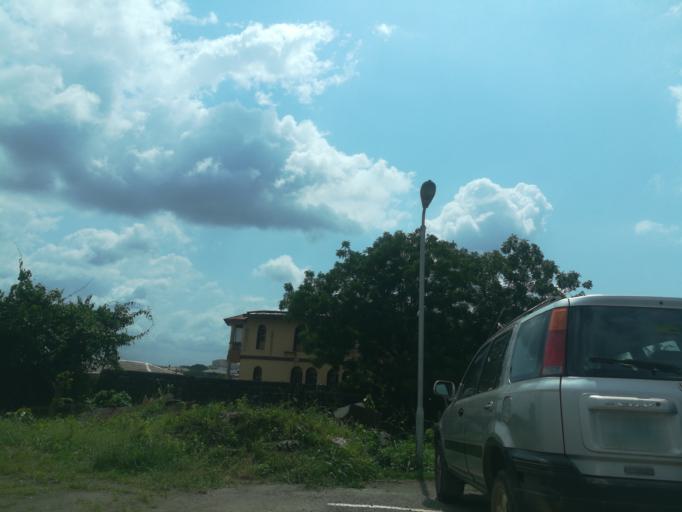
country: NG
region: Oyo
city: Ibadan
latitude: 7.3610
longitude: 3.8659
